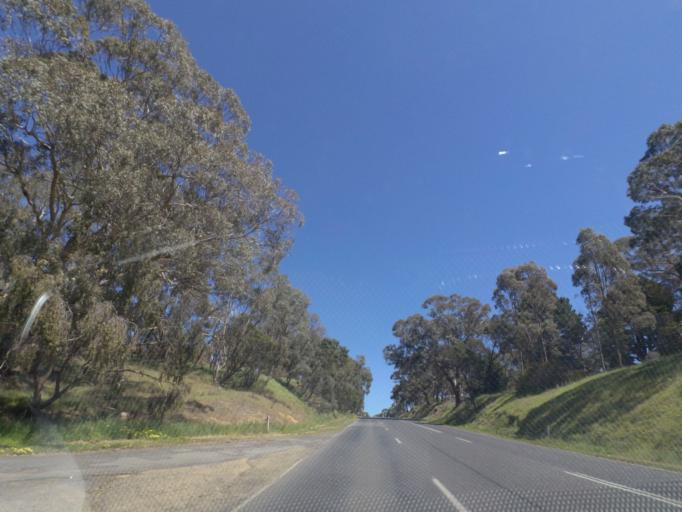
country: AU
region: Victoria
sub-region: Whittlesea
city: Whittlesea
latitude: -37.2875
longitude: 144.9669
